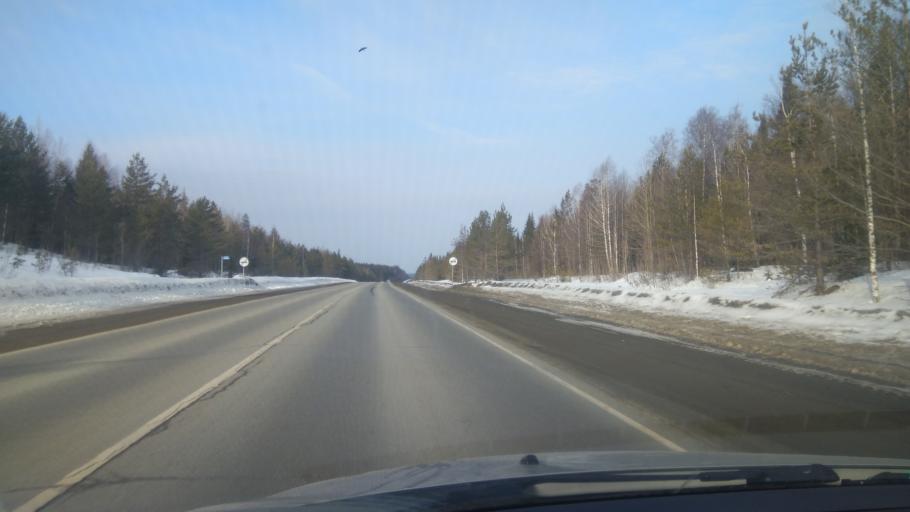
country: RU
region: Sverdlovsk
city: Nizhniye Sergi
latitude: 56.8251
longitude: 59.2439
